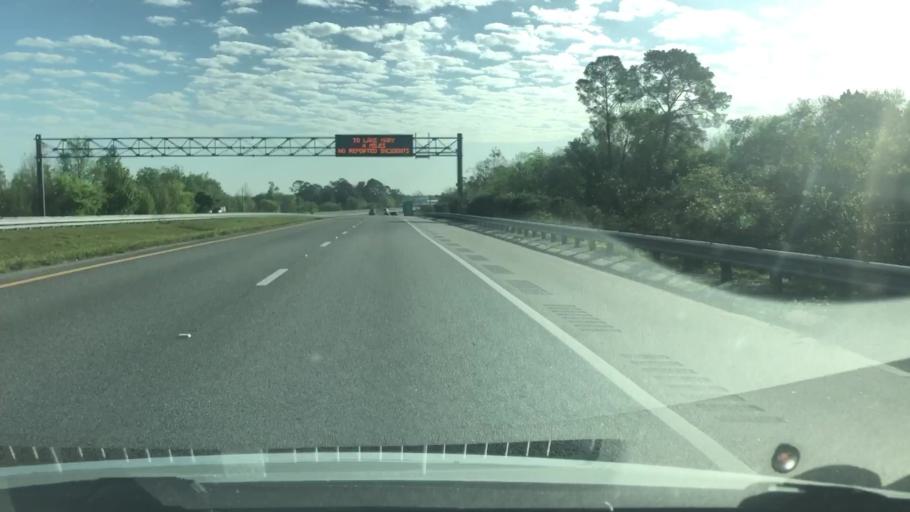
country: US
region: Florida
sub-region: Seminole County
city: Lake Mary
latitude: 28.8008
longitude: -81.3163
